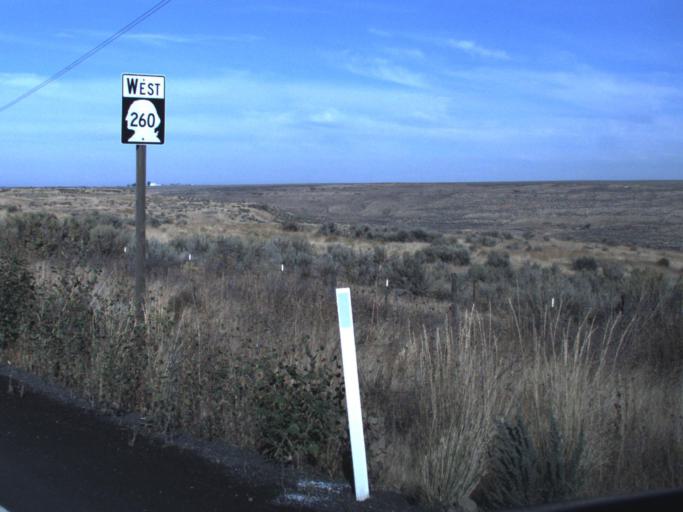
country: US
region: Washington
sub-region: Franklin County
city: Connell
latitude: 46.6299
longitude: -118.7327
